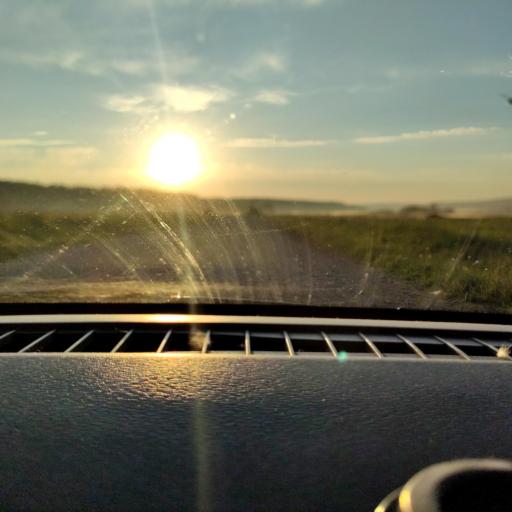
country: RU
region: Perm
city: Sylva
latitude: 57.8415
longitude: 56.7001
